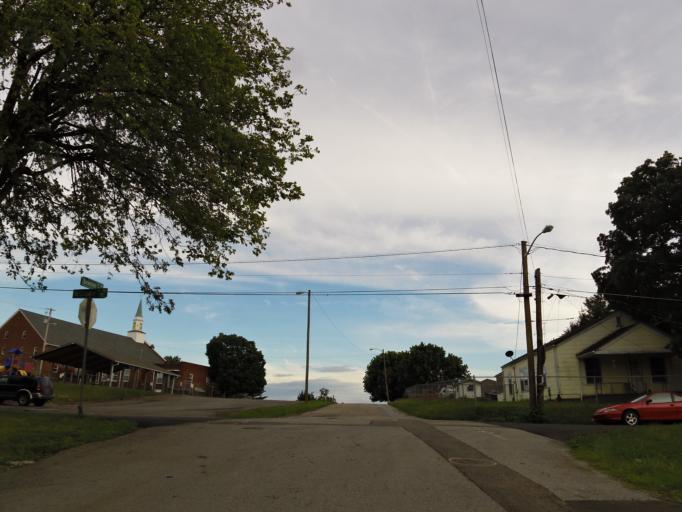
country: US
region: Tennessee
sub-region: Knox County
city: Knoxville
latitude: 35.9965
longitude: -83.9124
